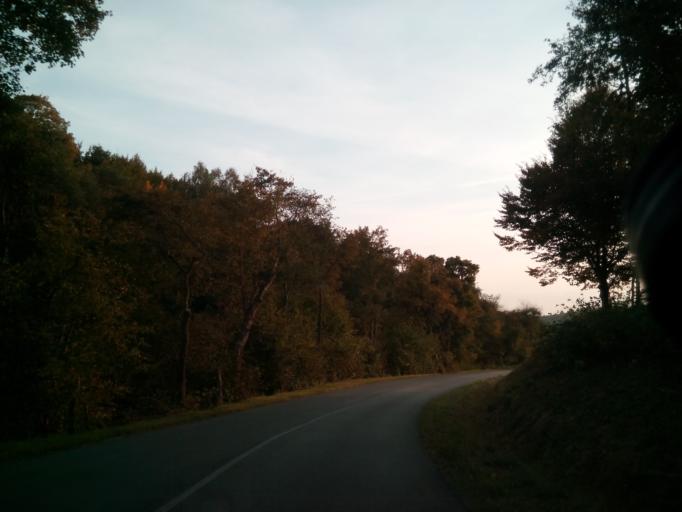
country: SK
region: Presovsky
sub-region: Okres Bardejov
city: Bardejov
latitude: 49.3497
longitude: 21.3408
